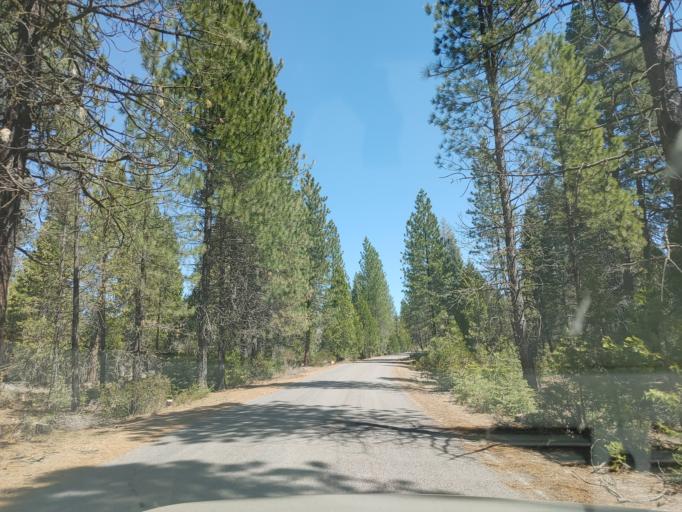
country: US
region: California
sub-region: Siskiyou County
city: McCloud
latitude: 41.2480
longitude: -121.9611
